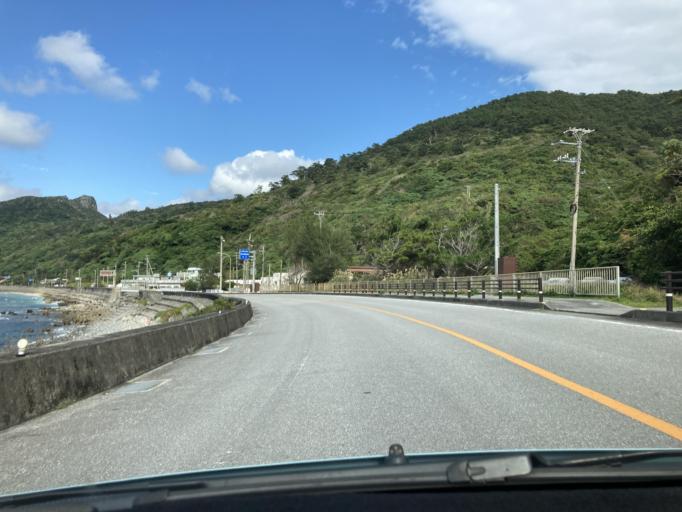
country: JP
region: Okinawa
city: Nago
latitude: 26.8395
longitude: 128.2522
